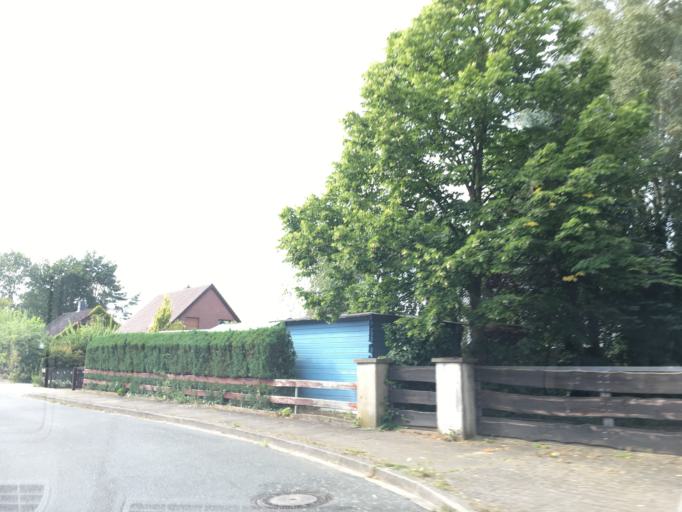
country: DE
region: Lower Saxony
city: Melbeck
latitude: 53.2158
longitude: 10.3931
